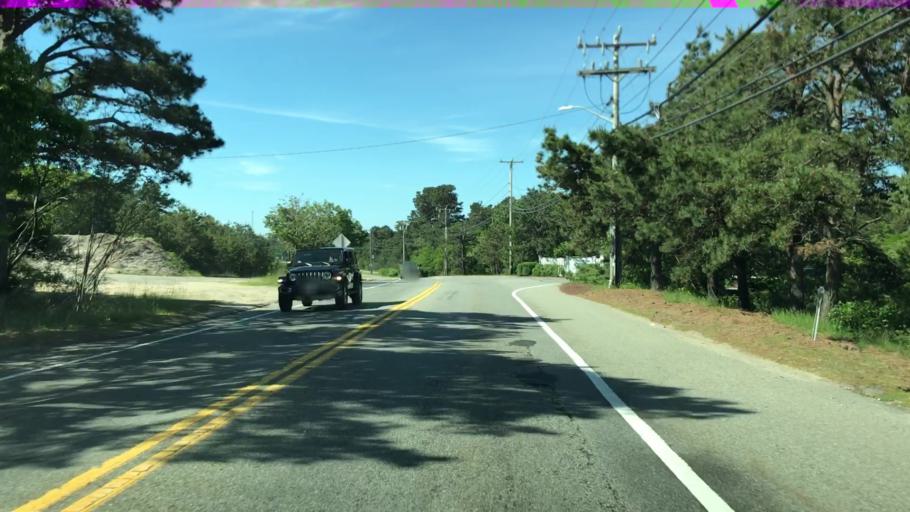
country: US
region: Massachusetts
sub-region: Barnstable County
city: Mashpee
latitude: 41.6163
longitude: -70.4887
